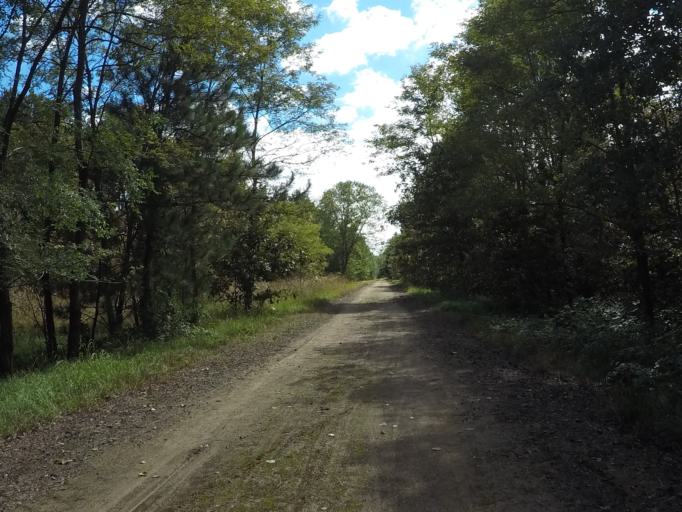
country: US
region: Wisconsin
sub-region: Sauk County
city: Spring Green
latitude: 43.1877
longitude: -90.2159
